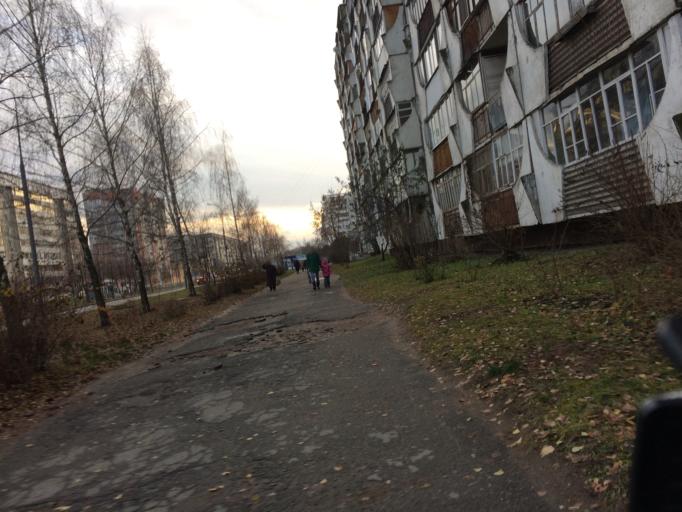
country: RU
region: Mariy-El
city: Yoshkar-Ola
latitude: 56.6326
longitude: 47.9188
